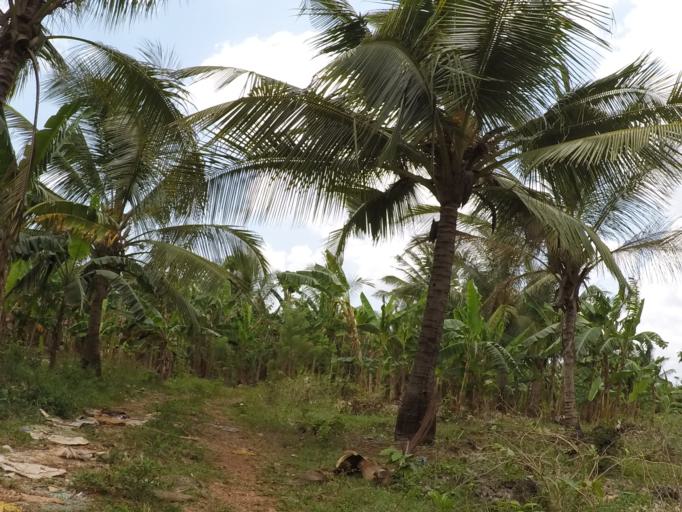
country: TZ
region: Zanzibar Central/South
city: Koani
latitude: -6.1716
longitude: 39.3083
